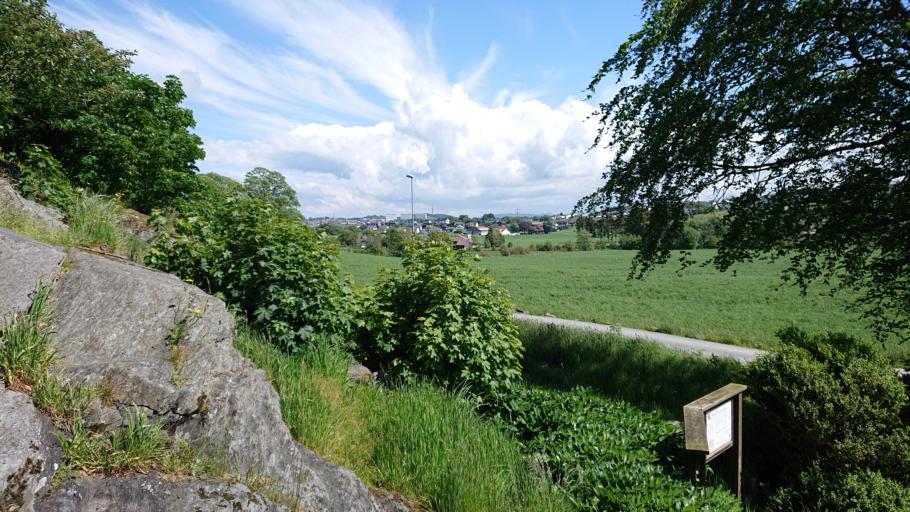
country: NO
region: Rogaland
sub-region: Randaberg
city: Randaberg
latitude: 58.9482
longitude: 5.6363
